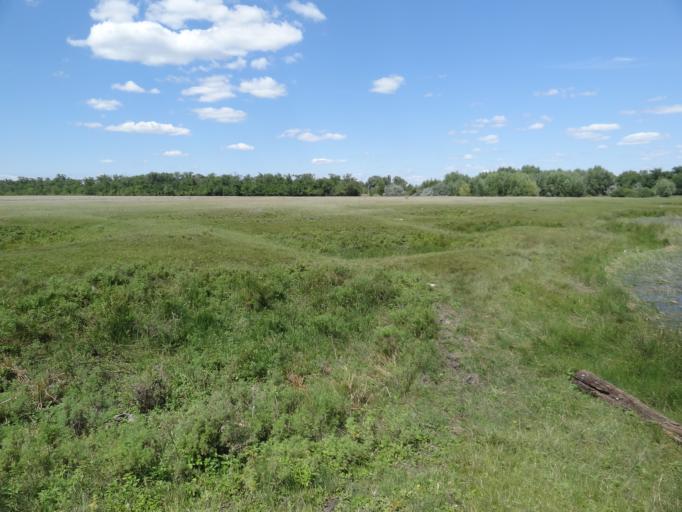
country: RU
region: Saratov
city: Sovetskoye
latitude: 51.2911
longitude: 46.6550
